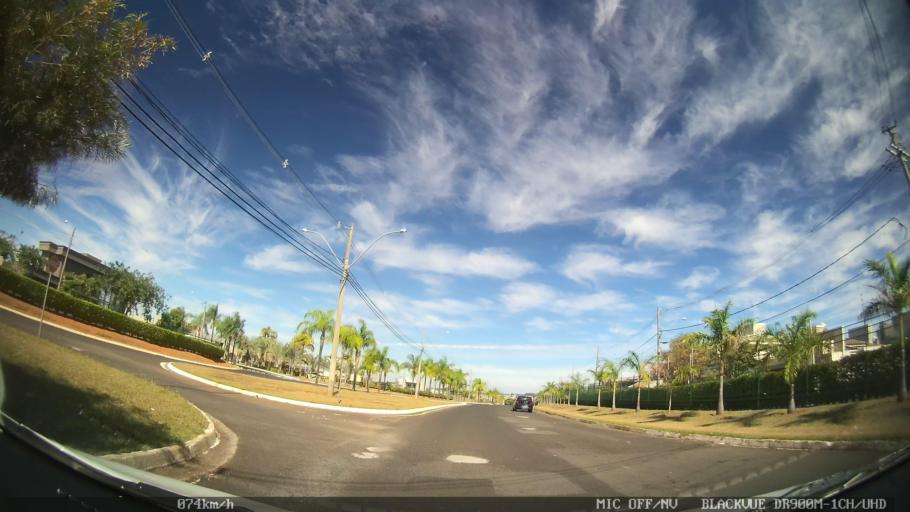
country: BR
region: Sao Paulo
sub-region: Bady Bassitt
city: Bady Bassitt
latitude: -20.8240
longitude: -49.4821
